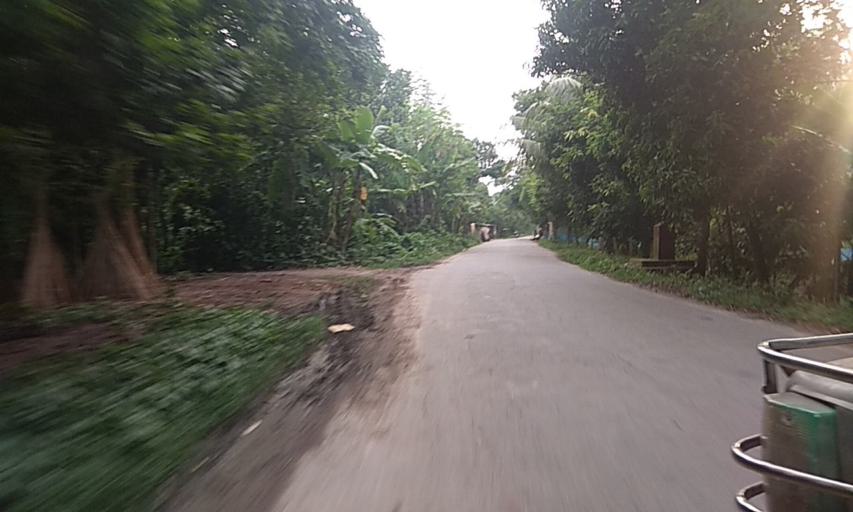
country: BD
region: Dhaka
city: Faridpur
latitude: 23.4590
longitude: 89.9799
